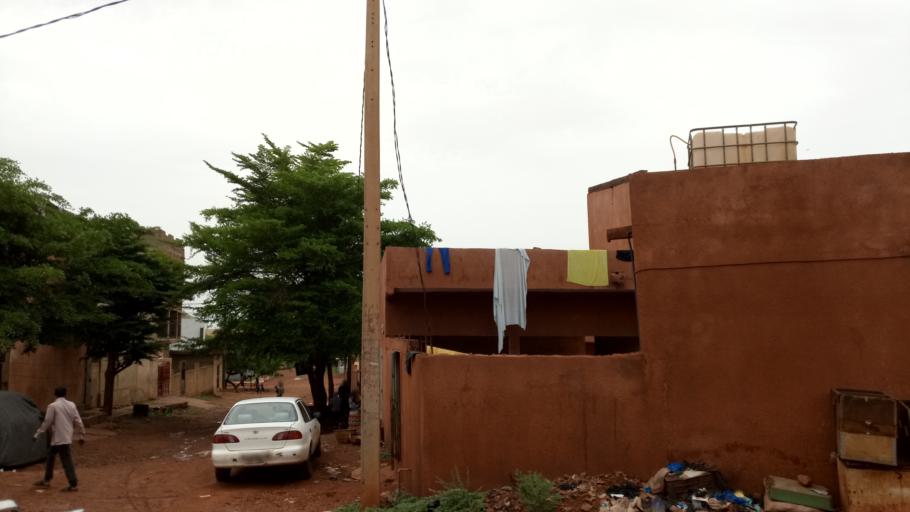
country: ML
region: Bamako
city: Bamako
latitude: 12.5873
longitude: -7.9961
